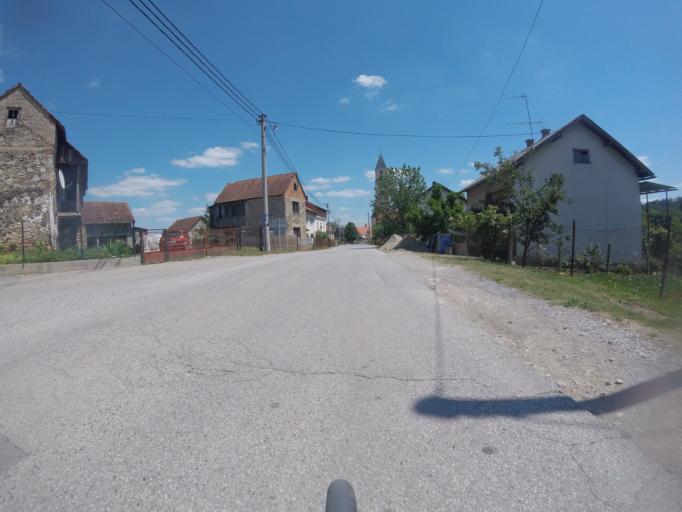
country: HR
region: Karlovacka
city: Ozalj
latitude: 45.6555
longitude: 15.5157
